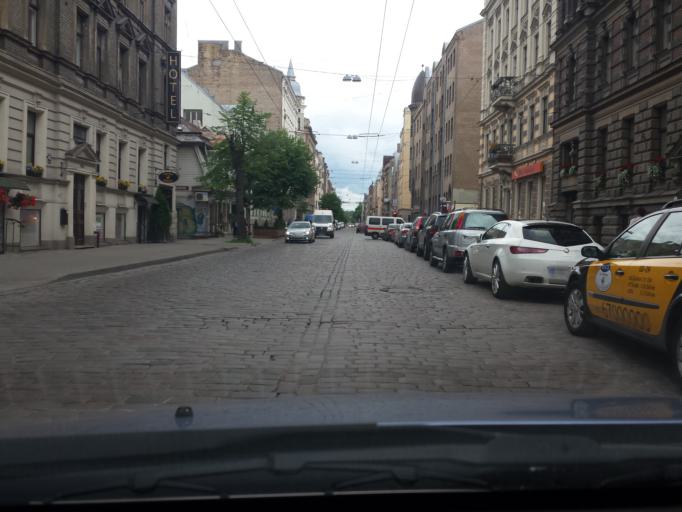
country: LV
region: Riga
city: Riga
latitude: 56.9539
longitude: 24.1290
